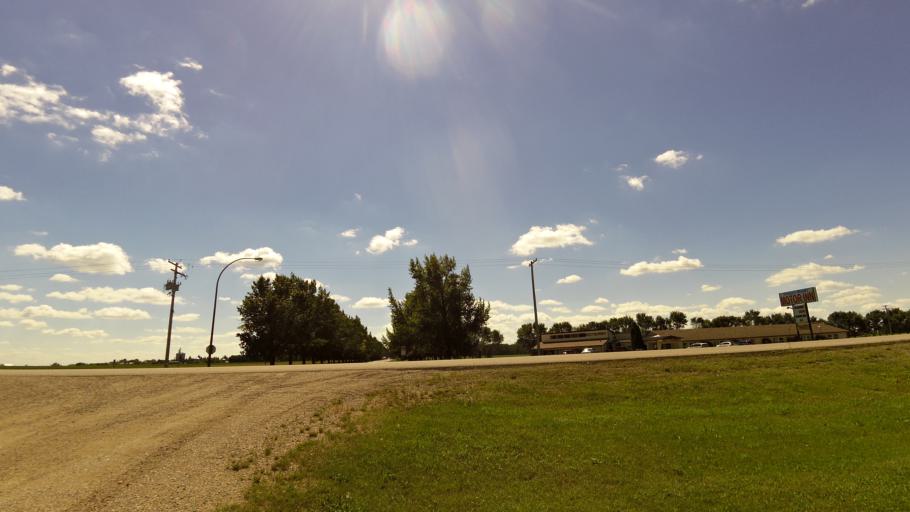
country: CA
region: Saskatchewan
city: Unity
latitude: 52.7551
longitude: -109.0201
